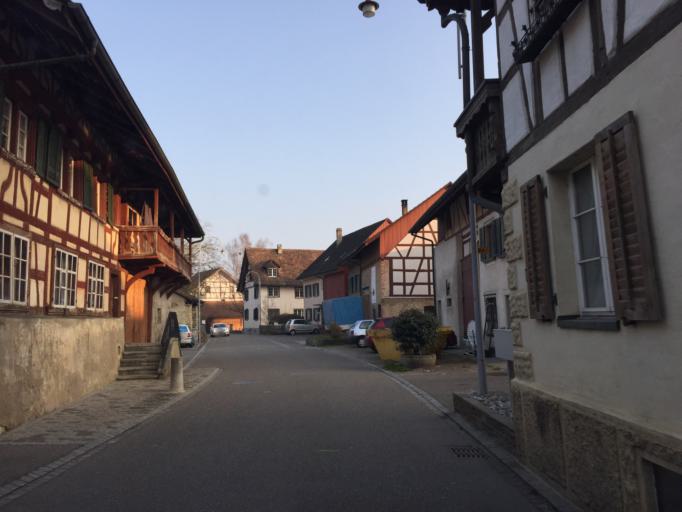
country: CH
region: Zurich
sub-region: Bezirk Andelfingen
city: Dachsen
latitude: 47.6644
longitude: 8.6184
